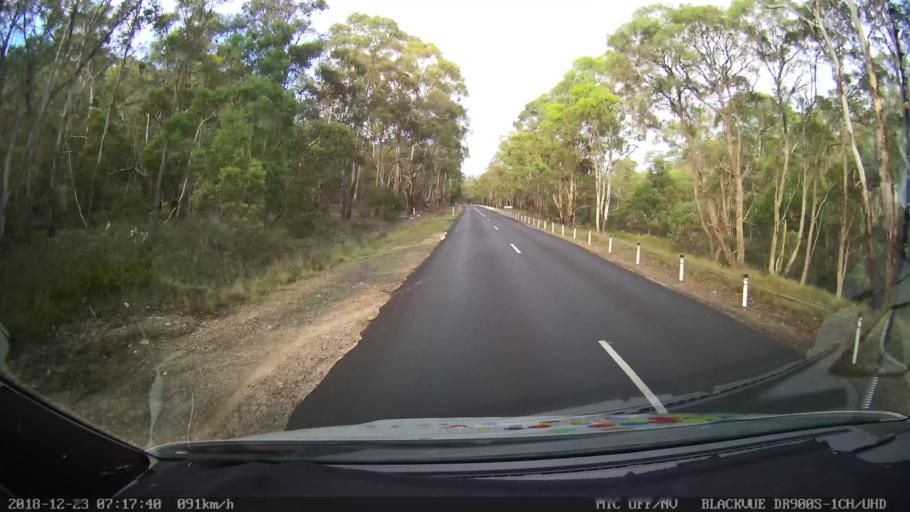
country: AU
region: New South Wales
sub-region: Bellingen
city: Dorrigo
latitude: -30.4683
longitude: 152.3007
